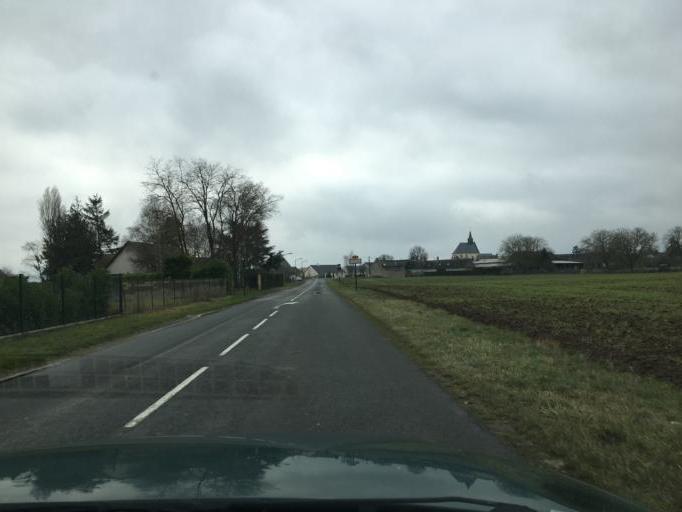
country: FR
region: Centre
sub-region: Departement du Loiret
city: Bricy
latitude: 48.0216
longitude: 1.7984
